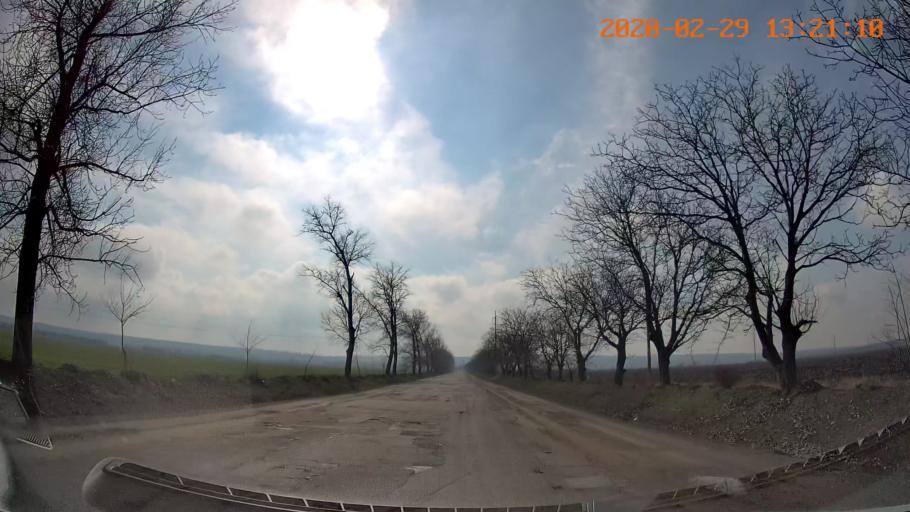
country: MD
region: Telenesti
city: Camenca
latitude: 47.9727
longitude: 28.6354
